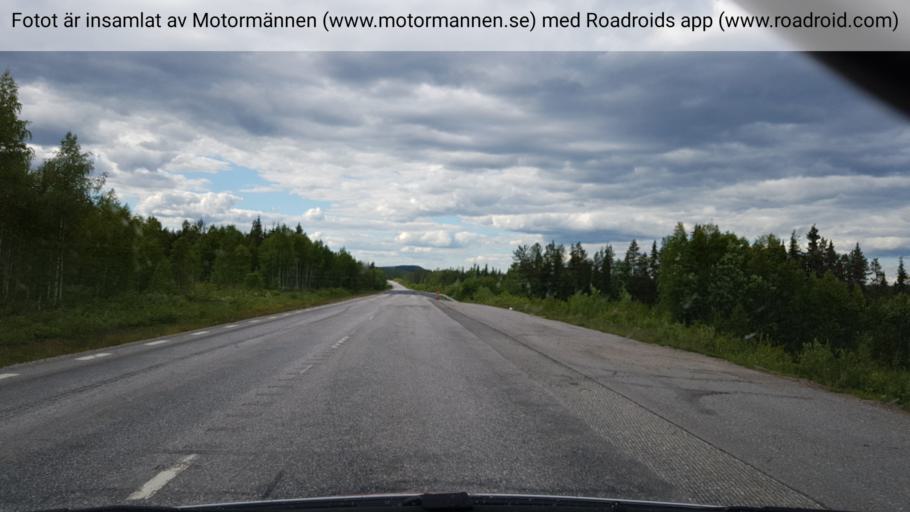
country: SE
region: Norrbotten
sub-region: Overkalix Kommun
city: OEverkalix
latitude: 66.6223
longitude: 22.2271
